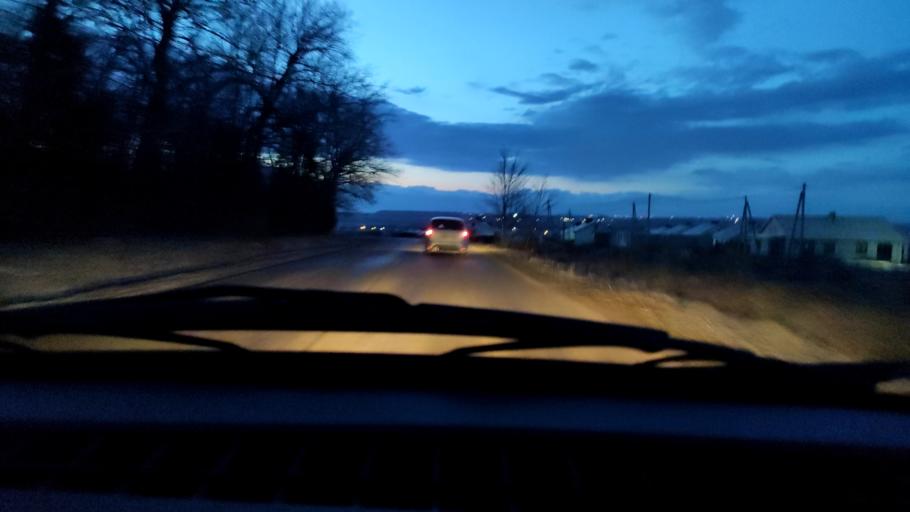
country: RU
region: Bashkortostan
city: Avdon
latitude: 54.4766
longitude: 55.8704
